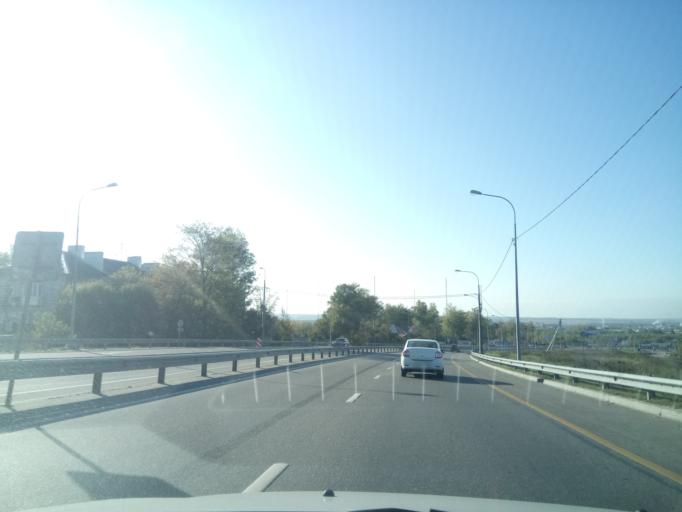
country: RU
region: Nizjnij Novgorod
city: Burevestnik
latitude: 56.1905
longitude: 43.9242
